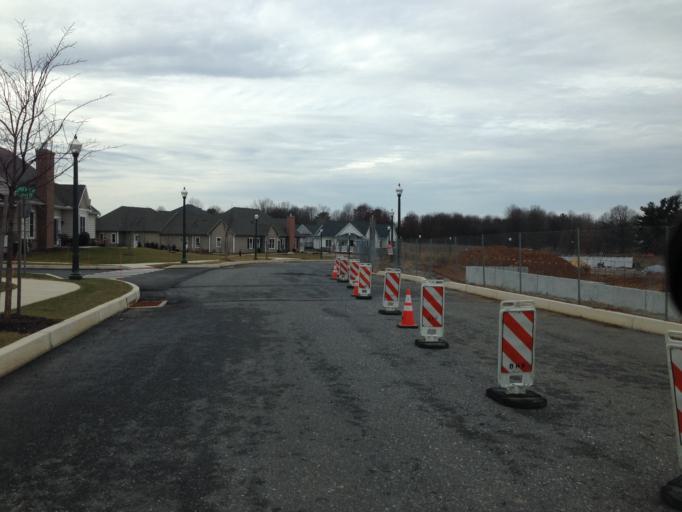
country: US
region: Pennsylvania
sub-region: Lancaster County
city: Lititz
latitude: 40.1485
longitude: -76.3166
